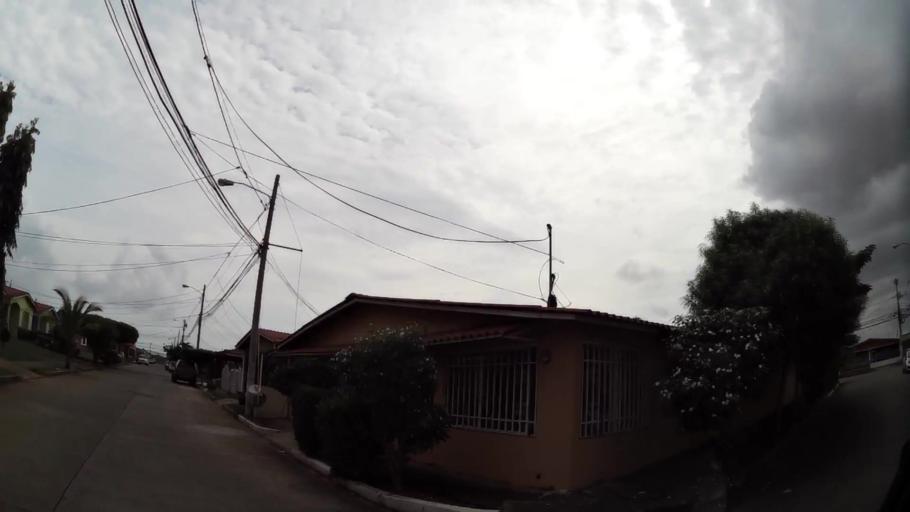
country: PA
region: Panama
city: Tocumen
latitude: 9.0486
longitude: -79.4069
